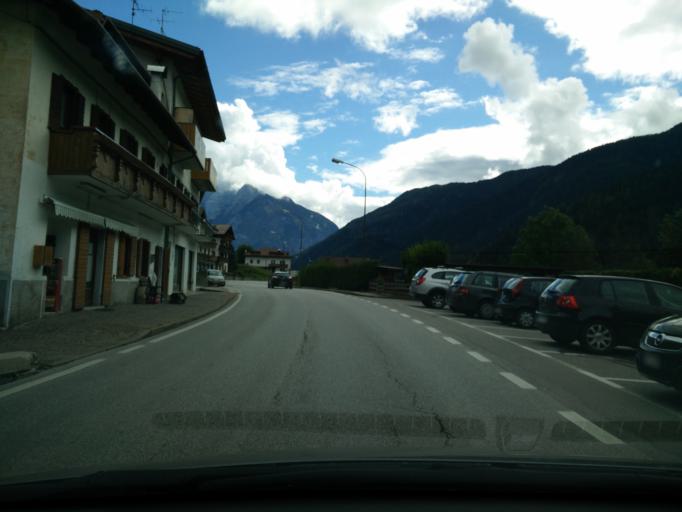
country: IT
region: Veneto
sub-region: Provincia di Belluno
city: Auronzo
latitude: 46.5607
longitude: 12.4198
